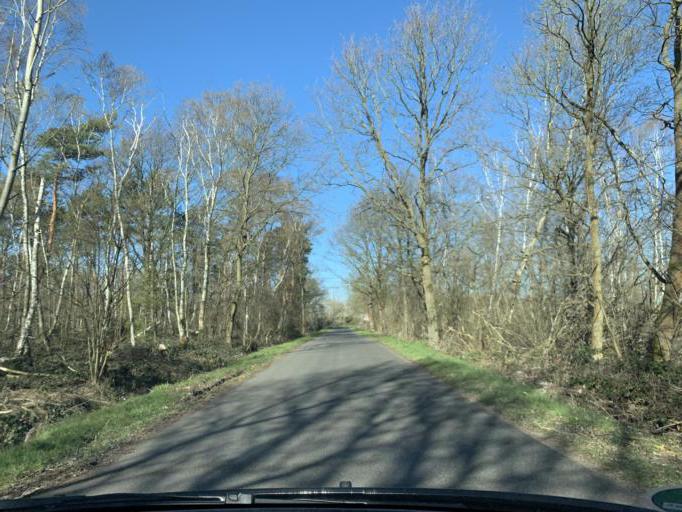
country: DE
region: North Rhine-Westphalia
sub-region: Regierungsbezirk Koln
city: Nideggen
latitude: 50.7090
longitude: 6.5423
